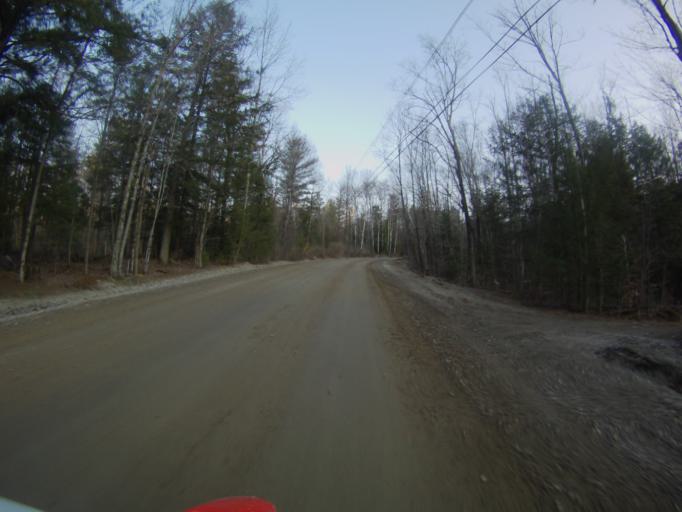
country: US
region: Vermont
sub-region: Addison County
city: Bristol
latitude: 44.0703
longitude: -73.0576
